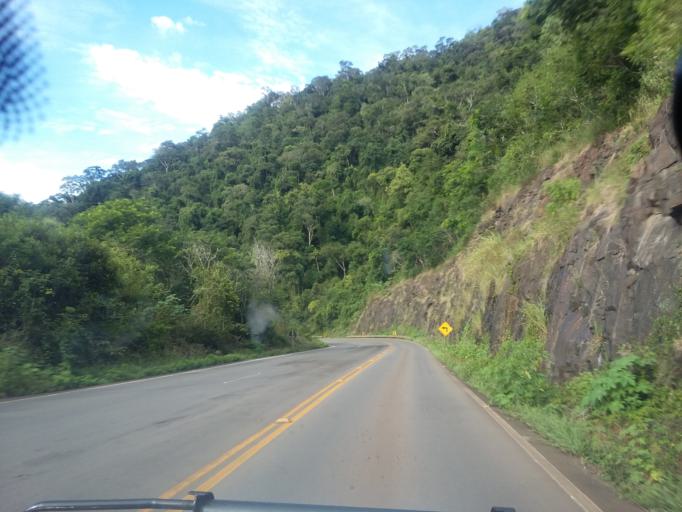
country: BR
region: Santa Catarina
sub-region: Celso Ramos
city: Celso Ramos
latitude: -27.6089
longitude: -51.4699
